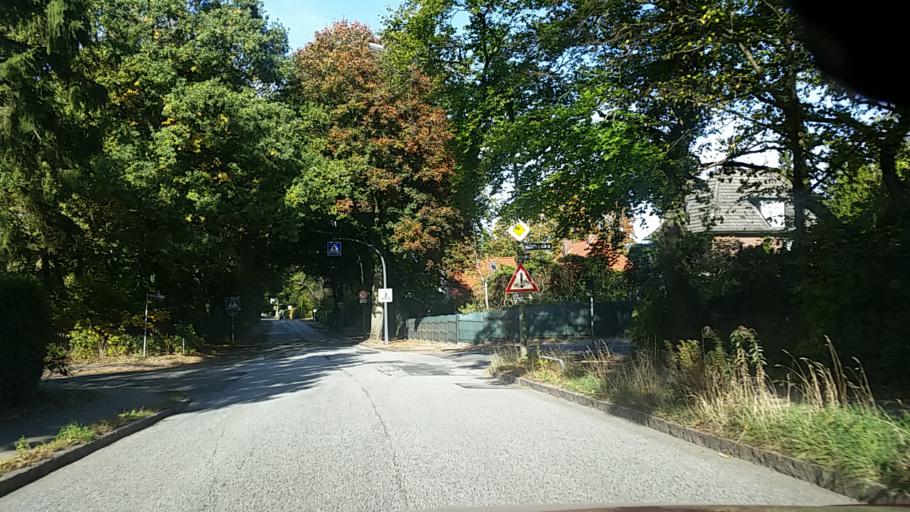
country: DE
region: Schleswig-Holstein
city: Halstenbek
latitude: 53.5713
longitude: 9.8082
